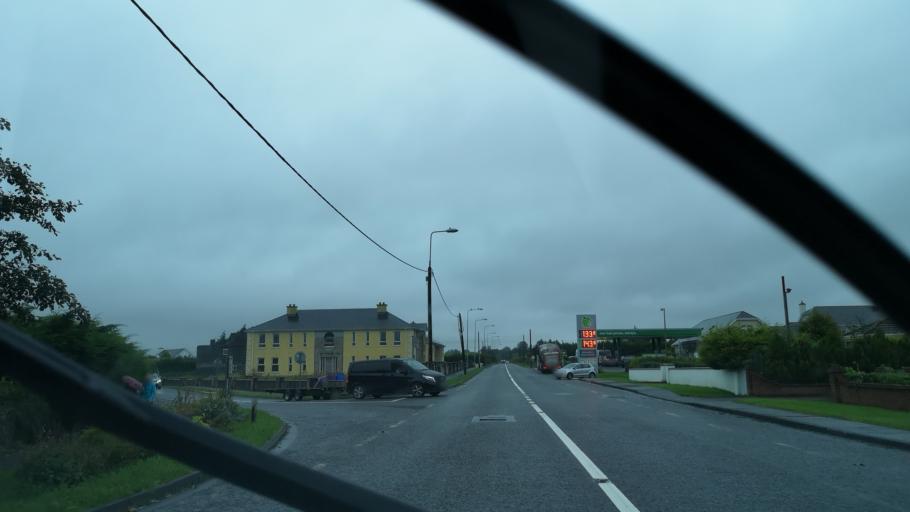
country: IE
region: Connaught
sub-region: Roscommon
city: Ballaghaderreen
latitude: 53.9058
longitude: -8.5879
